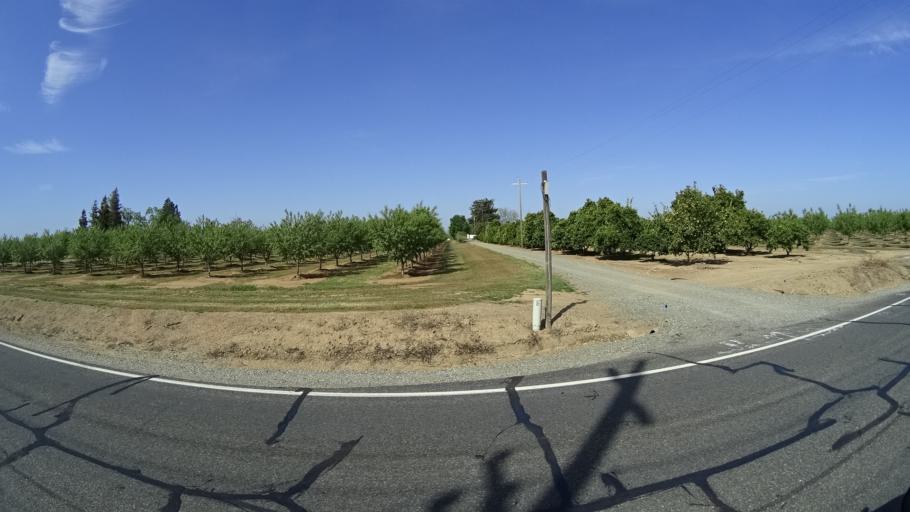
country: US
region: California
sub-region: Glenn County
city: Hamilton City
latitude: 39.6649
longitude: -122.0084
